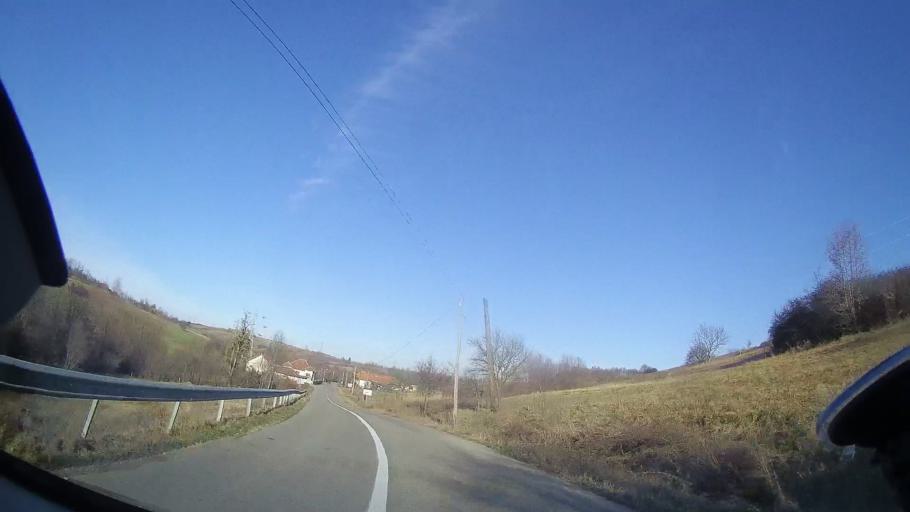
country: RO
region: Bihor
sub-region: Comuna Bratca
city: Bratca
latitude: 46.9368
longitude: 22.6044
